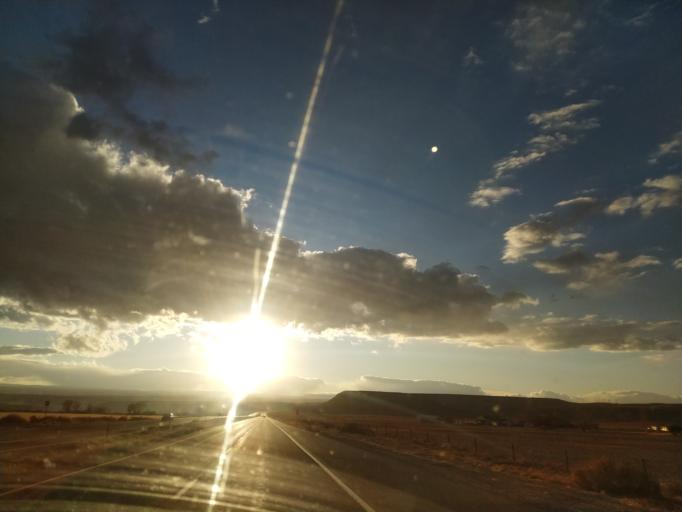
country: US
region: Colorado
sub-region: Delta County
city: Delta
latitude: 38.7582
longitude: -108.1433
